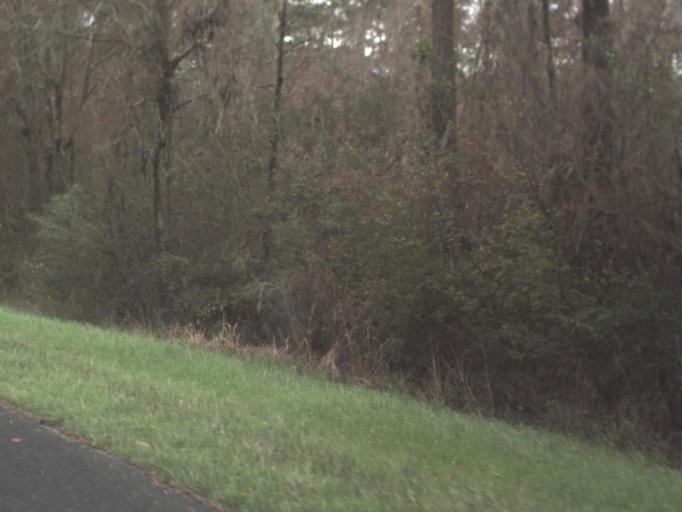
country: US
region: Florida
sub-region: Gadsden County
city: Havana
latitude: 30.5439
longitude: -84.3734
